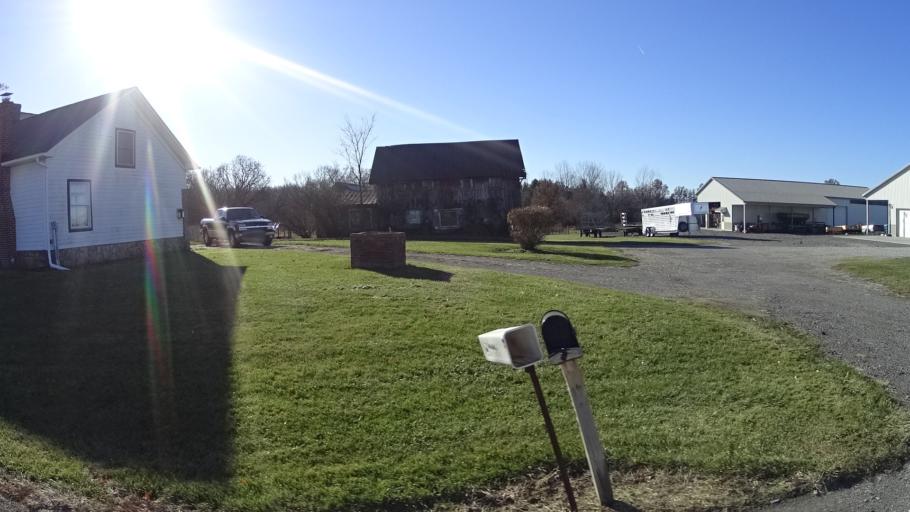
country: US
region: Ohio
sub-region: Lorain County
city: Oberlin
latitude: 41.3119
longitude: -82.1495
